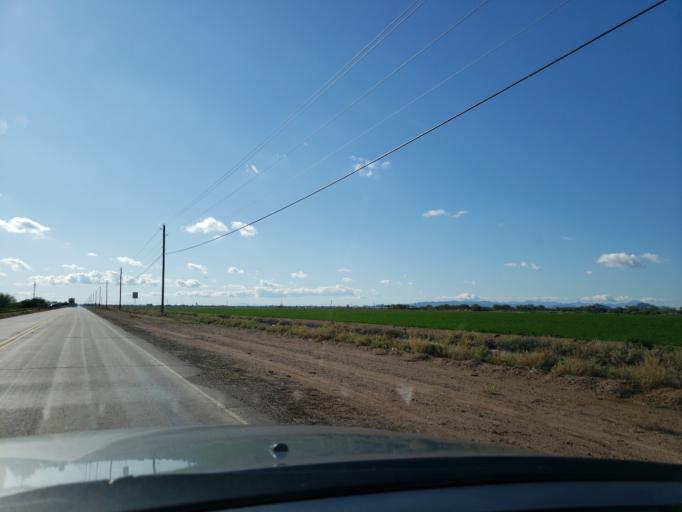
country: US
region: Arizona
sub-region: Maricopa County
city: Scottsdale
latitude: 33.5158
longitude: -111.8741
